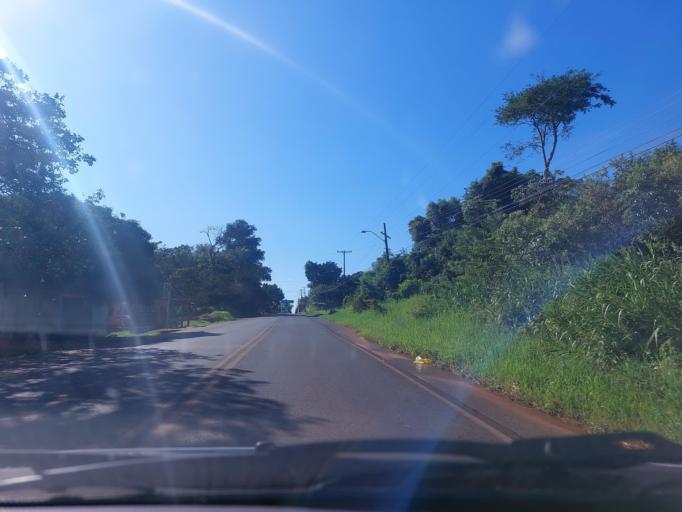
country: PY
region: San Pedro
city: Guayaybi
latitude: -24.5311
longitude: -56.4105
